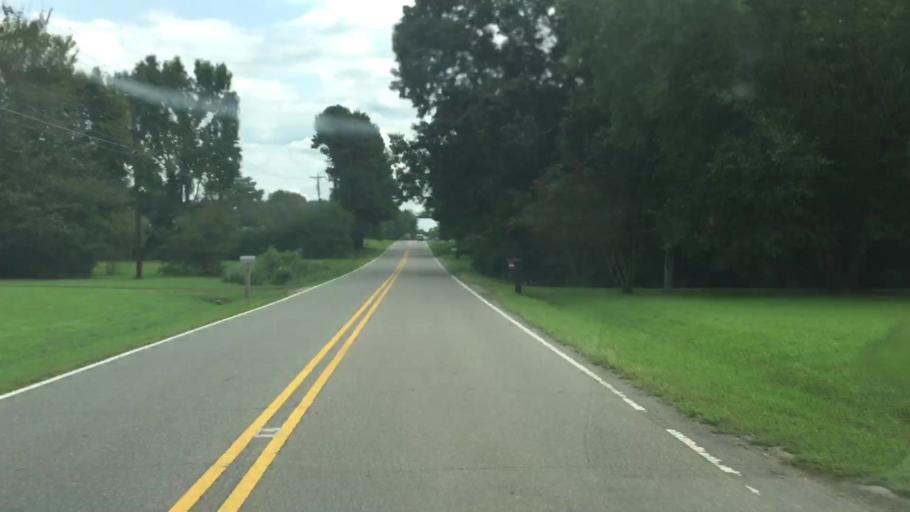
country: US
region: North Carolina
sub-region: Iredell County
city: Mooresville
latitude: 35.6063
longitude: -80.7507
